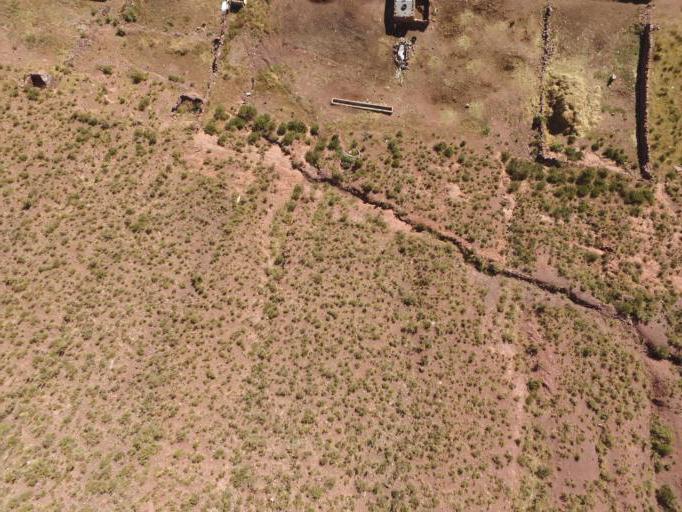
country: BO
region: Oruro
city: Challapata
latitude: -18.6933
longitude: -66.7559
